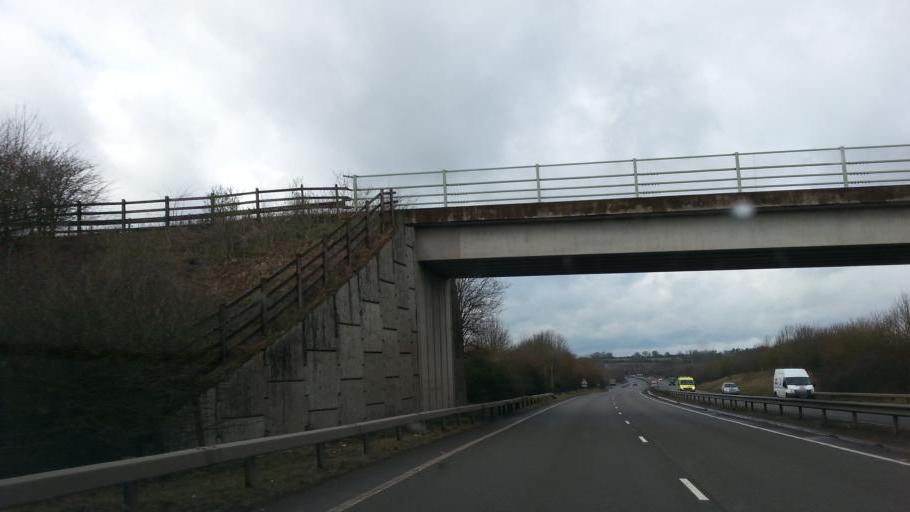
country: GB
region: England
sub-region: Leicestershire
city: Great Glen
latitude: 52.5645
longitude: -1.0293
